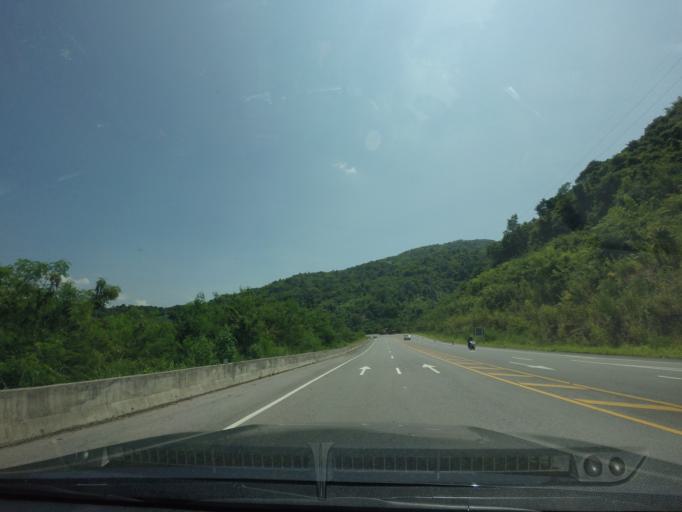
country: TH
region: Phetchabun
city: Lom Sak
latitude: 16.7724
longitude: 101.1258
